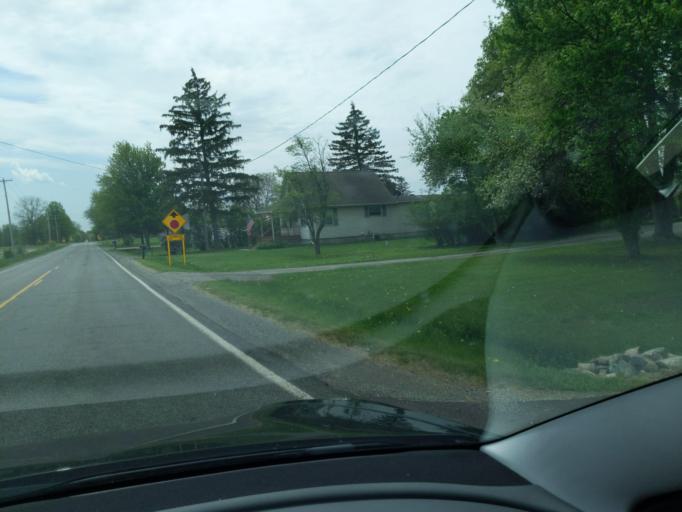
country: US
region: Michigan
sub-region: Ingham County
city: Holt
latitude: 42.5845
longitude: -84.5427
